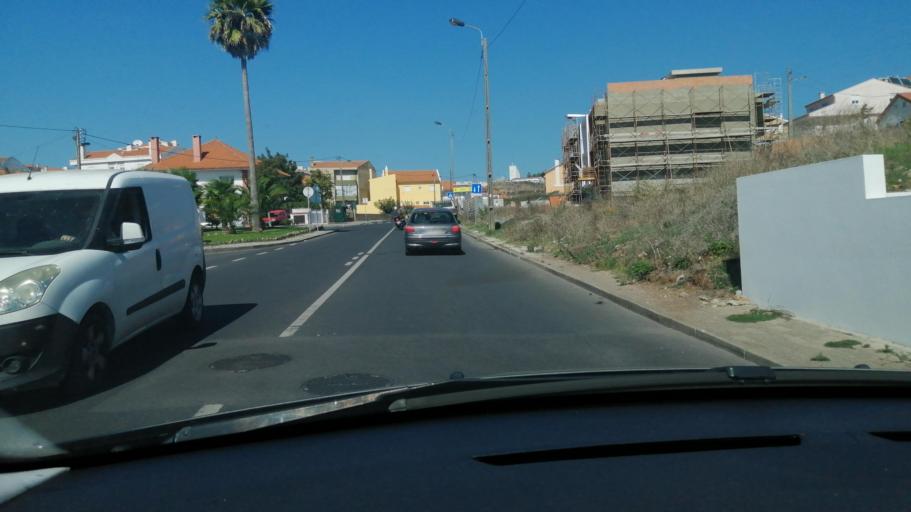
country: PT
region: Lisbon
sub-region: Odivelas
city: Canecas
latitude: 38.7984
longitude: -9.2267
